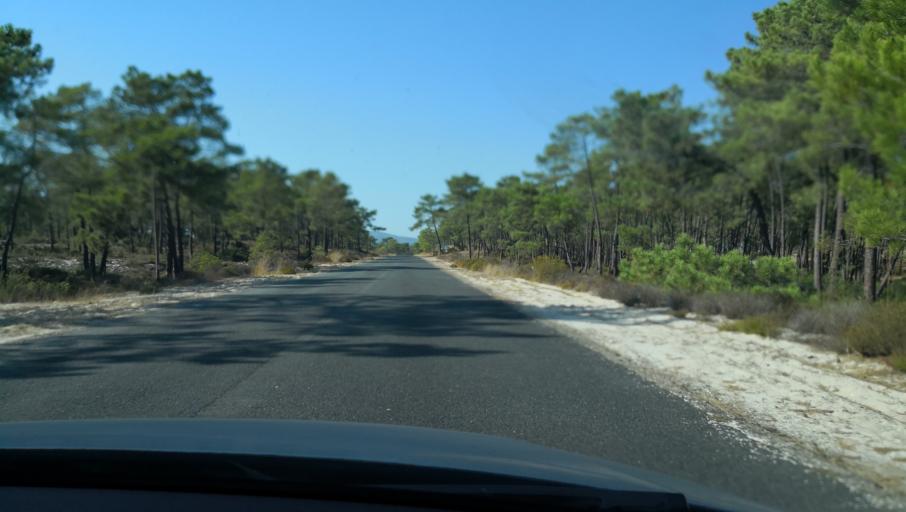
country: PT
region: Setubal
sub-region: Setubal
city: Setubal
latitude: 38.4696
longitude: -8.8710
